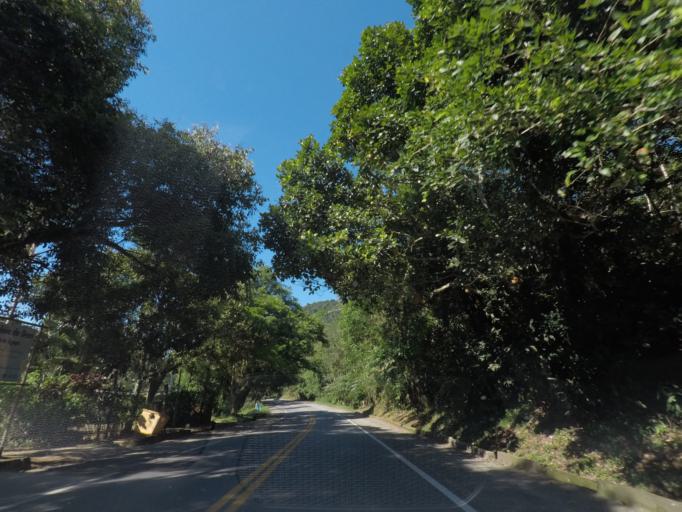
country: BR
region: Rio de Janeiro
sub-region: Parati
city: Paraty
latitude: -23.2833
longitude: -44.6938
